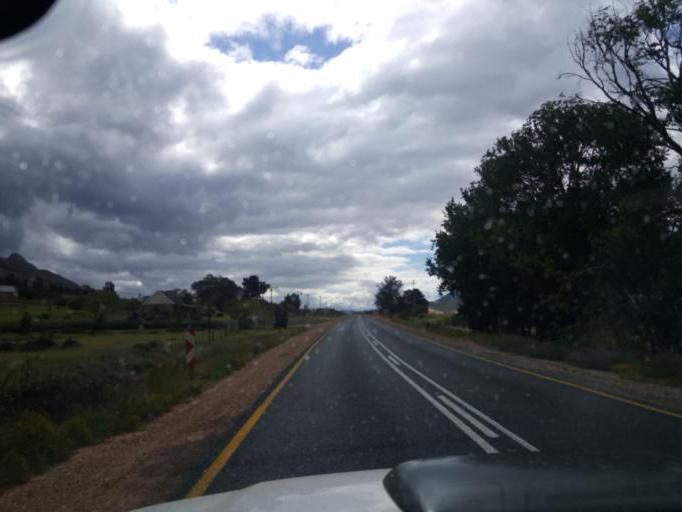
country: ZA
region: Western Cape
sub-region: Eden District Municipality
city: George
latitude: -33.8339
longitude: 22.4428
